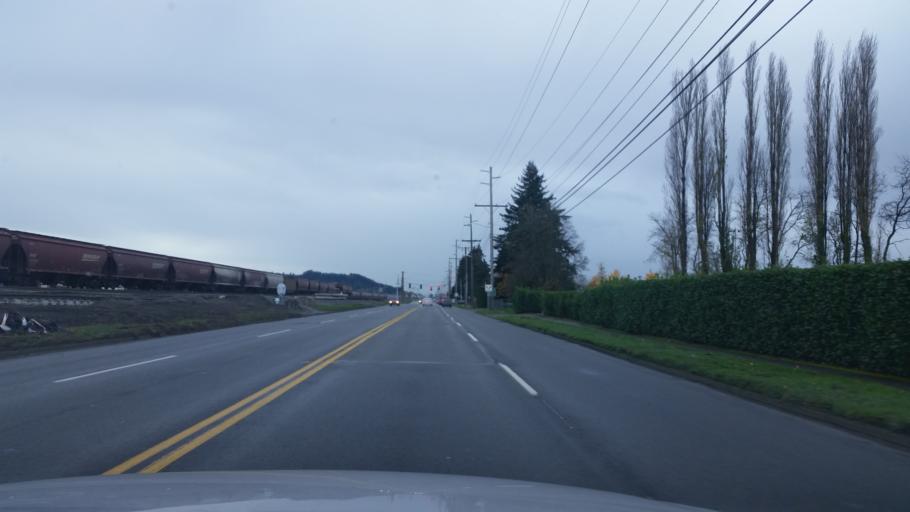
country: US
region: Washington
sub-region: King County
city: Auburn
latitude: 47.2986
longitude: -122.2323
